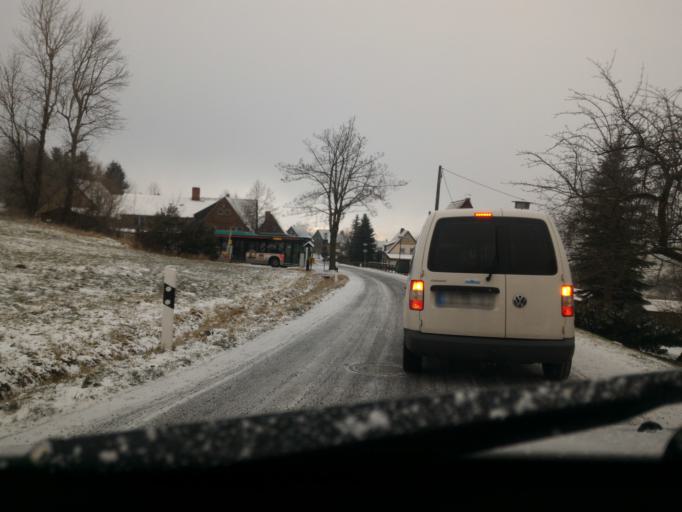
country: DE
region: Saxony
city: Kurort Jonsdorf
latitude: 50.8538
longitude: 14.6553
